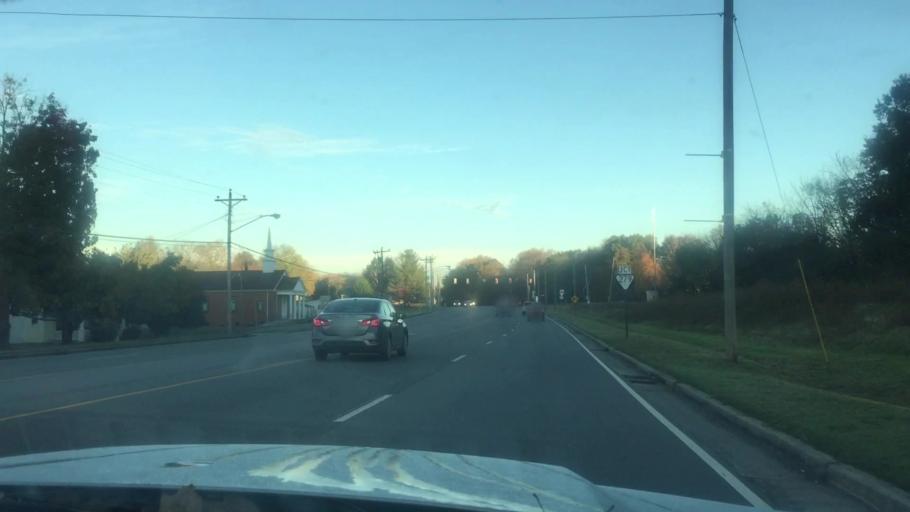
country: US
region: Tennessee
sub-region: Franklin County
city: Estill Springs
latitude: 35.2718
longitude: -86.1287
